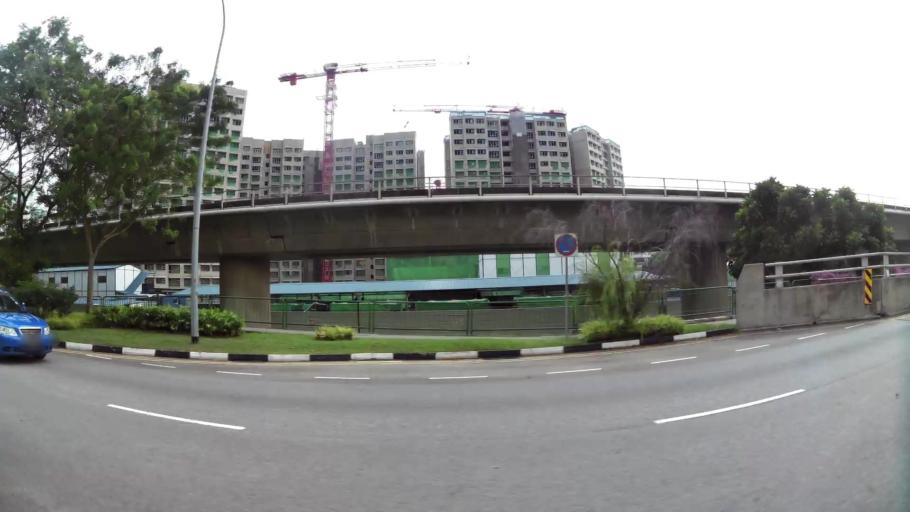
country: MY
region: Johor
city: Johor Bahru
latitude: 1.4476
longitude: 103.8130
